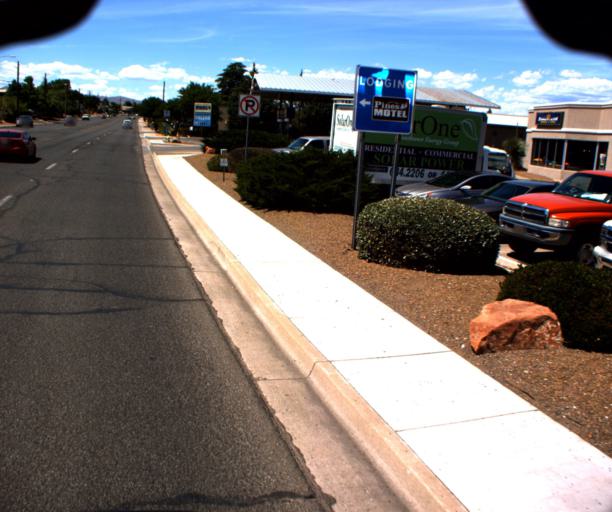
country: US
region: Arizona
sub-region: Yavapai County
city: Verde Village
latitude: 34.7229
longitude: -112.0046
